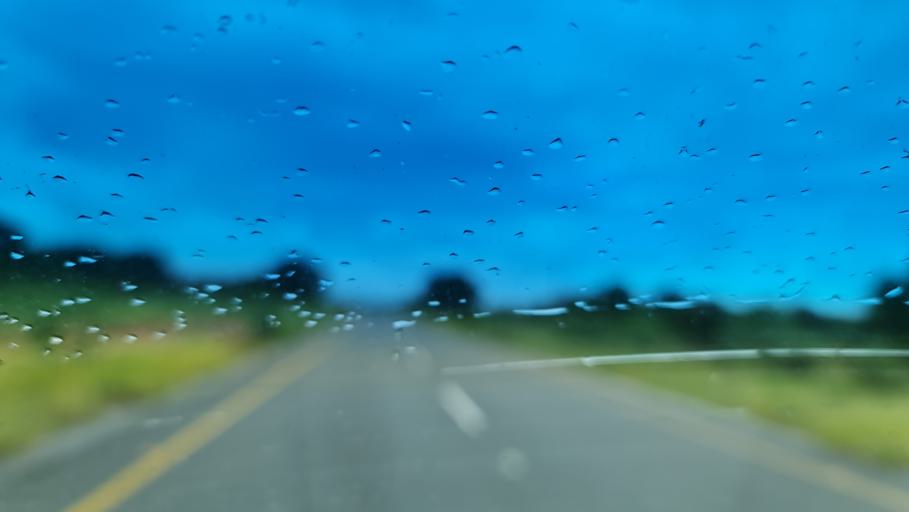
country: MZ
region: Nampula
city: Nampula
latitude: -15.5303
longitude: 39.3316
